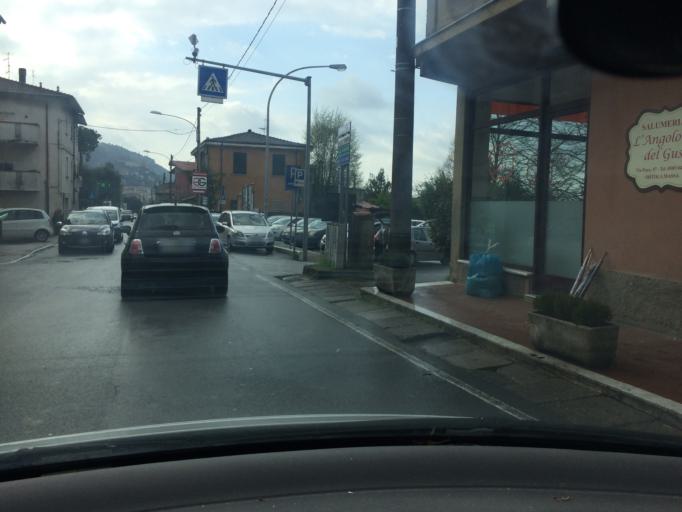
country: IT
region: Tuscany
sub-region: Provincia di Massa-Carrara
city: Massa
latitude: 44.0443
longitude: 10.1353
